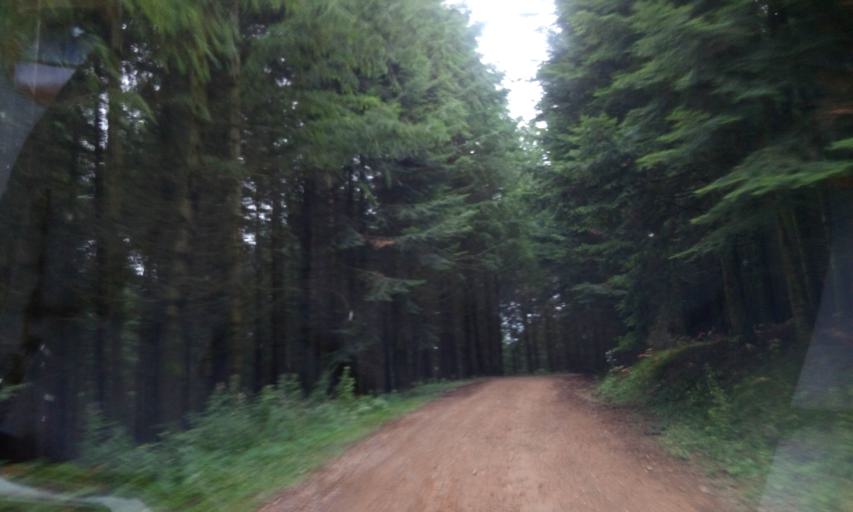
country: FR
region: Rhone-Alpes
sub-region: Departement du Rhone
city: Cublize
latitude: 46.0236
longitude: 4.4275
